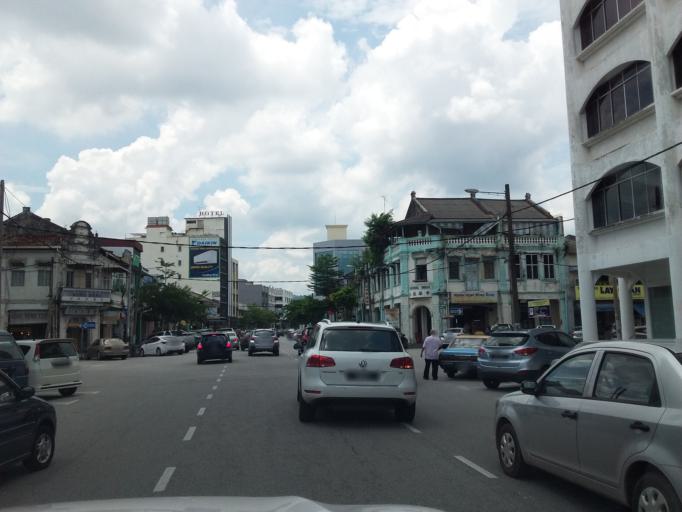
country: MY
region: Johor
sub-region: Daerah Batu Pahat
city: Batu Pahat
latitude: 1.8515
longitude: 102.9271
